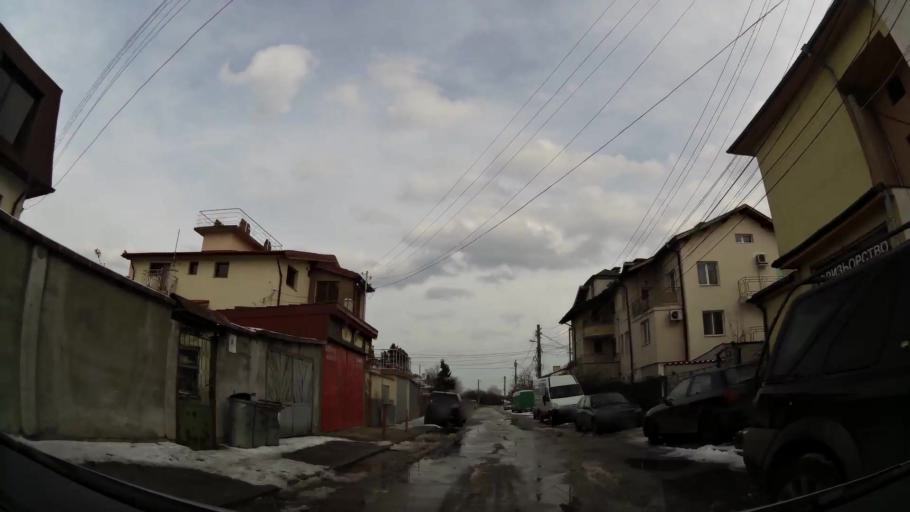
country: BG
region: Sofia-Capital
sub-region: Stolichna Obshtina
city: Sofia
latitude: 42.7012
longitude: 23.3860
